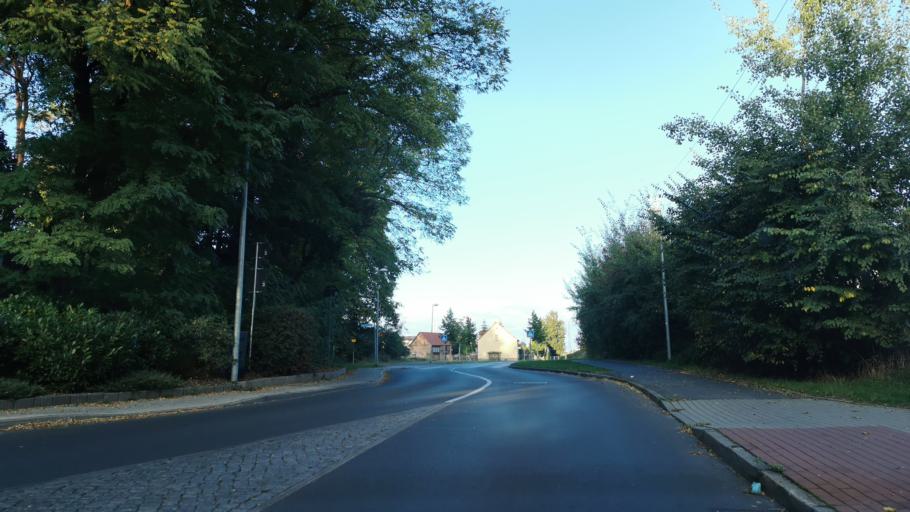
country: DE
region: Brandenburg
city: Michendorf
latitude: 52.3112
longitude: 13.0210
